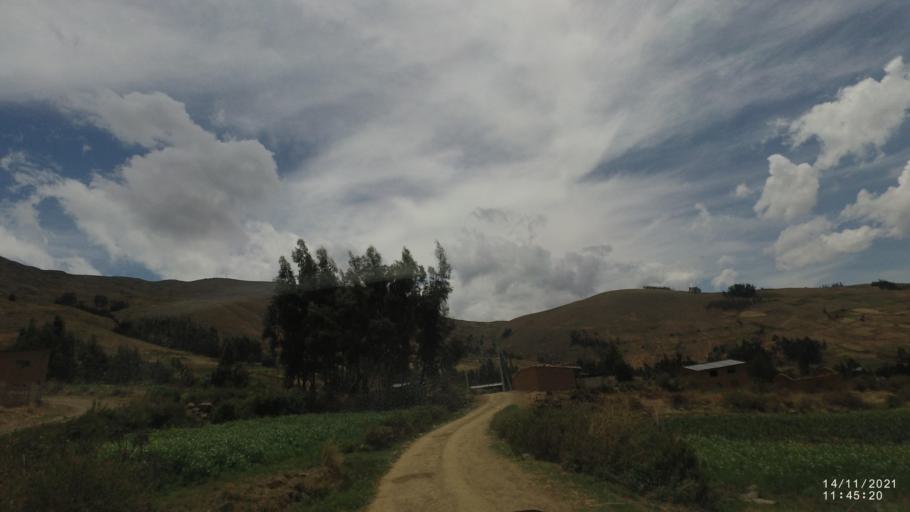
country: BO
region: Cochabamba
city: Colomi
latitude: -17.3532
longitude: -65.9891
